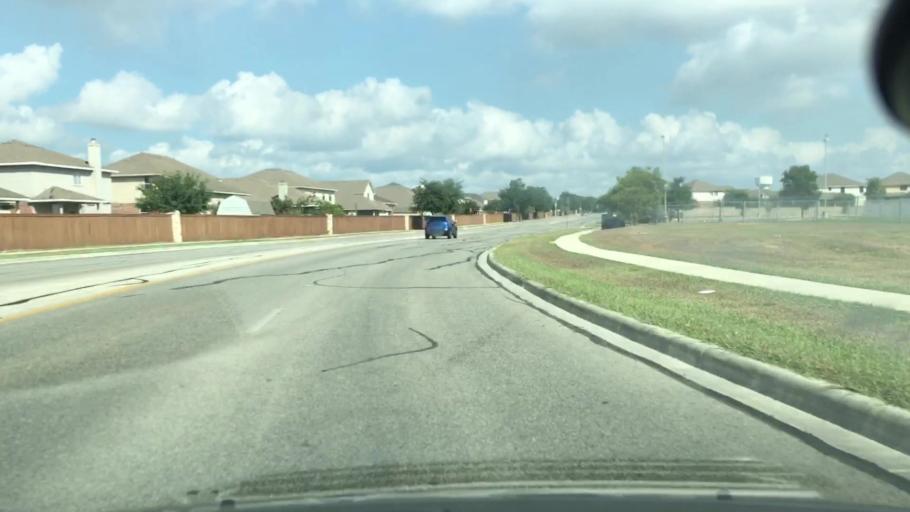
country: US
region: Texas
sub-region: Guadalupe County
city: Cibolo
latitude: 29.5727
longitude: -98.2409
